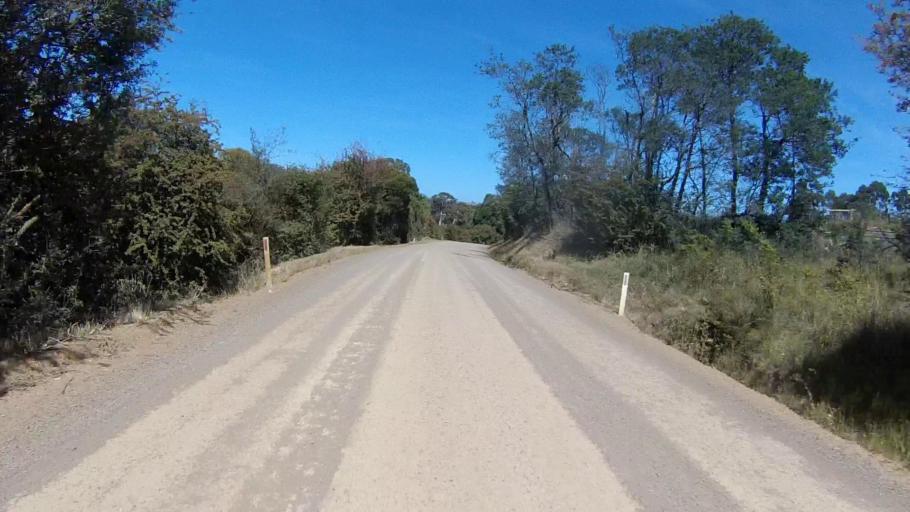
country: AU
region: Tasmania
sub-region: Sorell
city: Sorell
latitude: -42.7564
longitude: 147.6631
